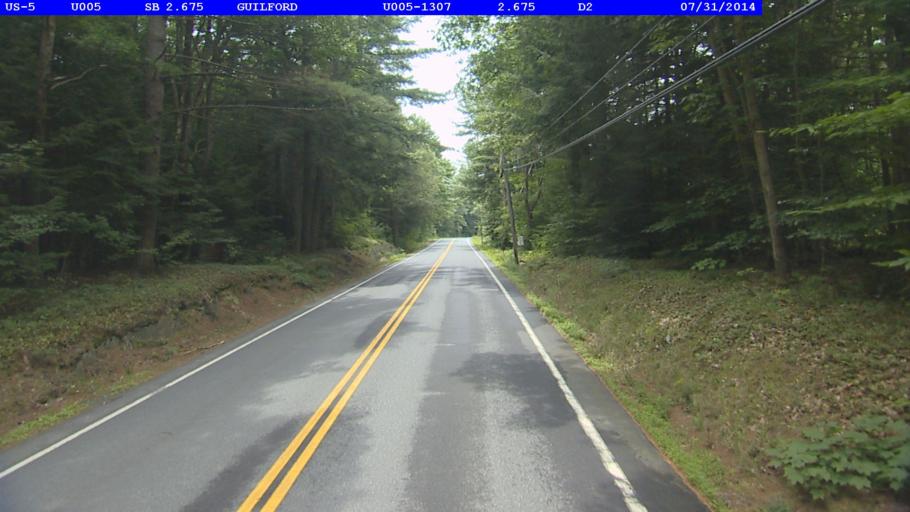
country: US
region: New Hampshire
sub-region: Cheshire County
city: Hinsdale
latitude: 42.7680
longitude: -72.5675
